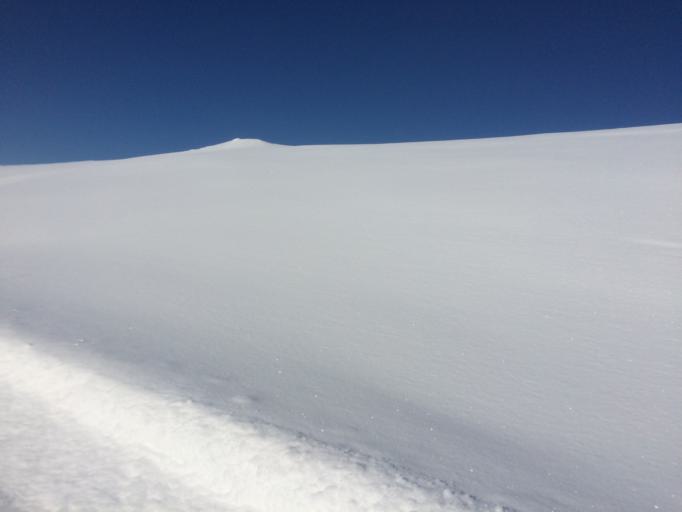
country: NO
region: Oppland
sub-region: Ringebu
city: Ringebu
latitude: 61.3707
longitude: 10.0745
